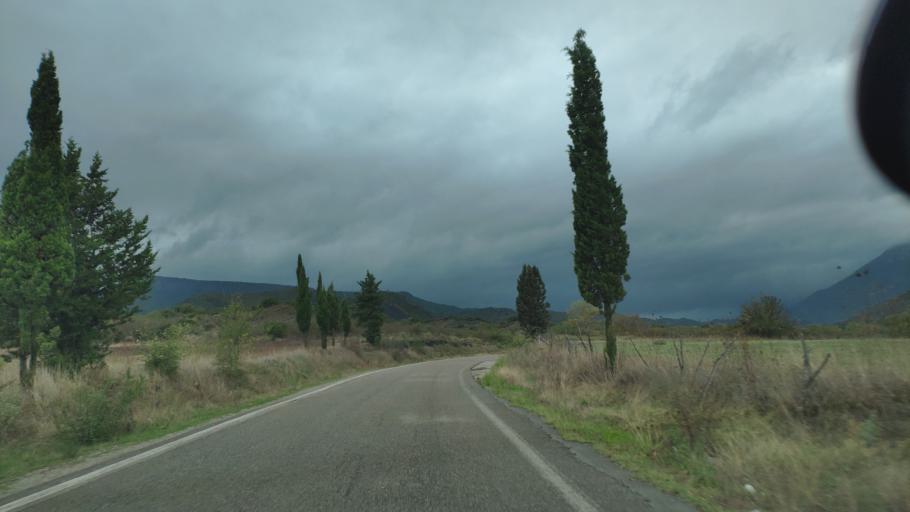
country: GR
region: West Greece
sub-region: Nomos Aitolias kai Akarnanias
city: Krikellos
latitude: 38.9784
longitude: 21.3247
